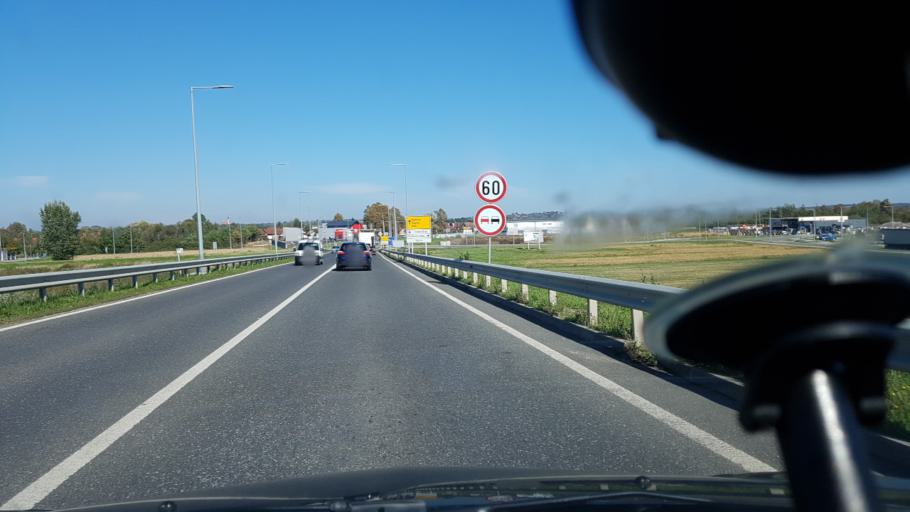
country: HR
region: Zagrebacka
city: Lupoglav
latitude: 45.7055
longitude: 16.4090
